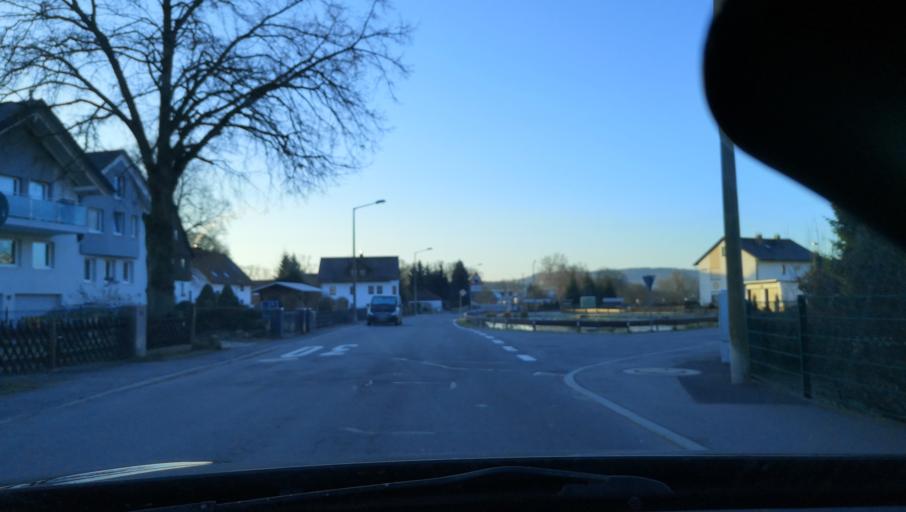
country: DE
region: Bavaria
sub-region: Upper Franconia
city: Neustadt bei Coburg
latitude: 50.3155
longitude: 11.1030
